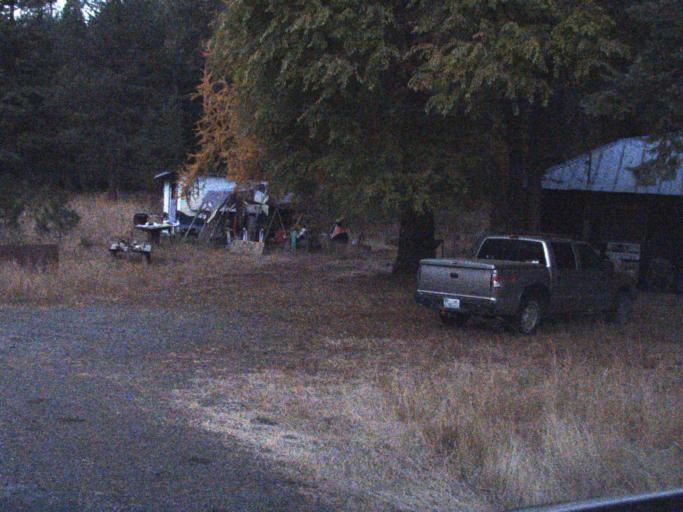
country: US
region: Washington
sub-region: Ferry County
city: Republic
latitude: 48.4684
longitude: -118.7523
